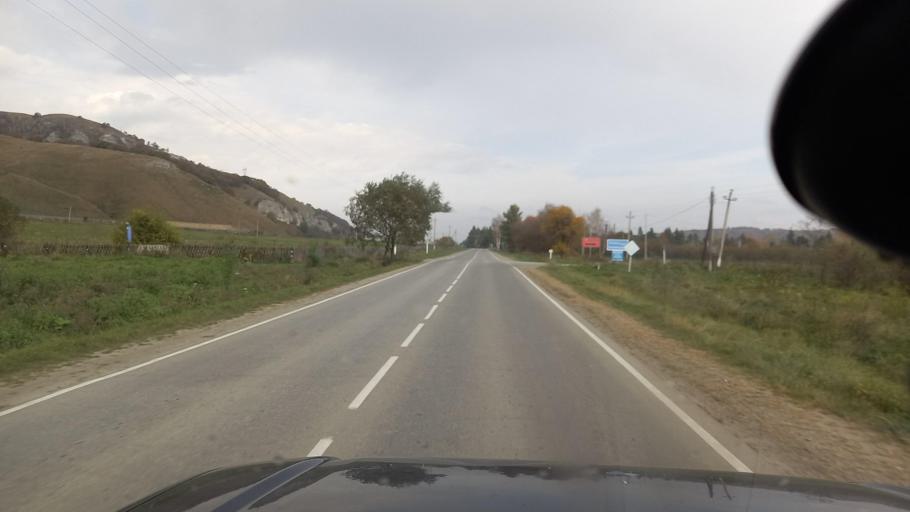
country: RU
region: Krasnodarskiy
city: Psebay
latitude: 44.1450
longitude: 40.8254
